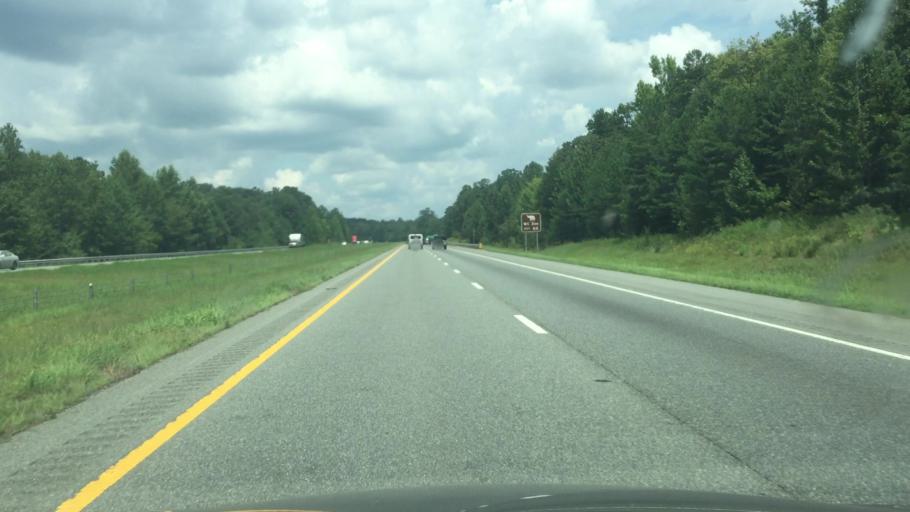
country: US
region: North Carolina
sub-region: Randolph County
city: Asheboro
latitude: 35.5777
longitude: -79.8063
